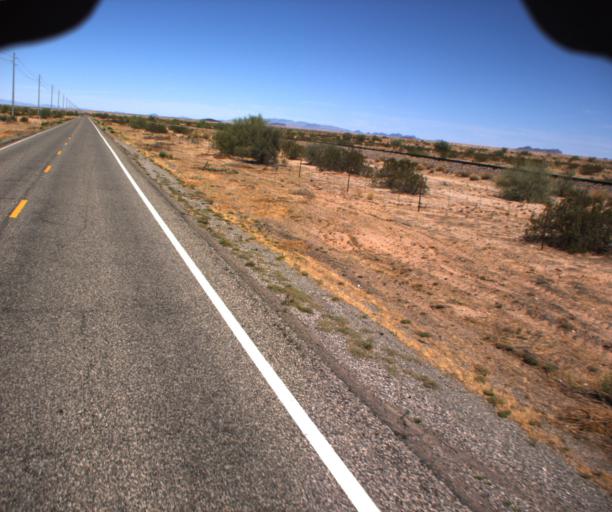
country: US
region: Arizona
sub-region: La Paz County
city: Cienega Springs
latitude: 33.9770
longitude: -114.0516
